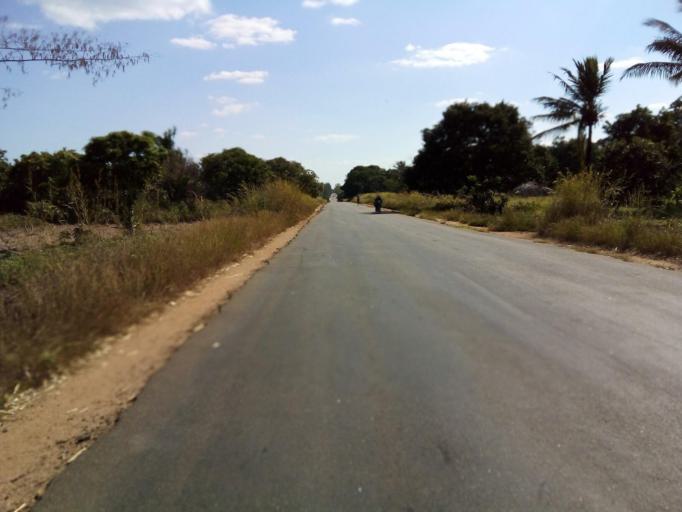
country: MZ
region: Zambezia
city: Quelimane
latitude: -17.5767
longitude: 36.6535
